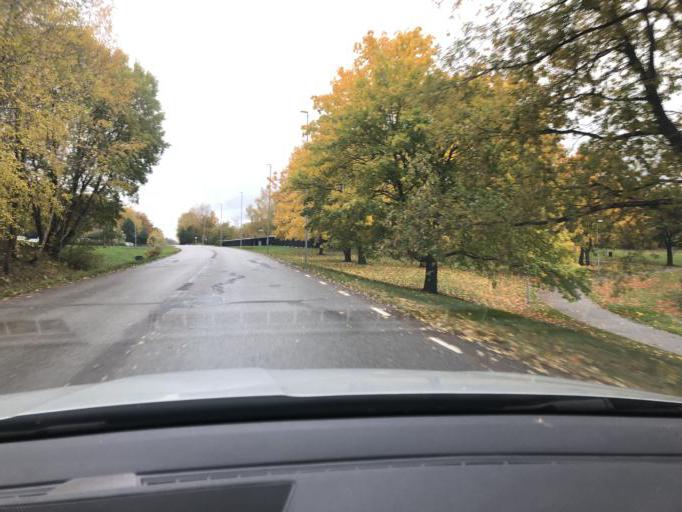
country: SE
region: Stockholm
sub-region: Botkyrka Kommun
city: Alby
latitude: 59.2334
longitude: 17.8597
